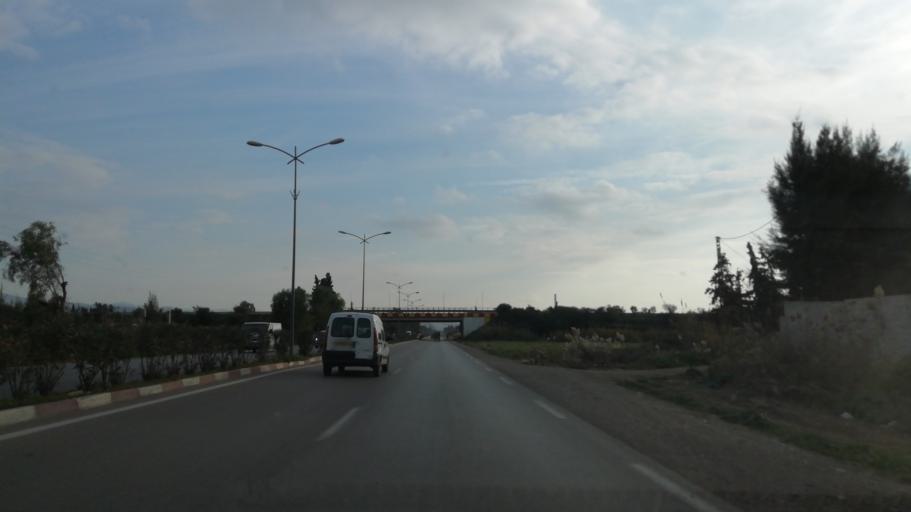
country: DZ
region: Mascara
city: Mascara
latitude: 35.6241
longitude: 0.0617
